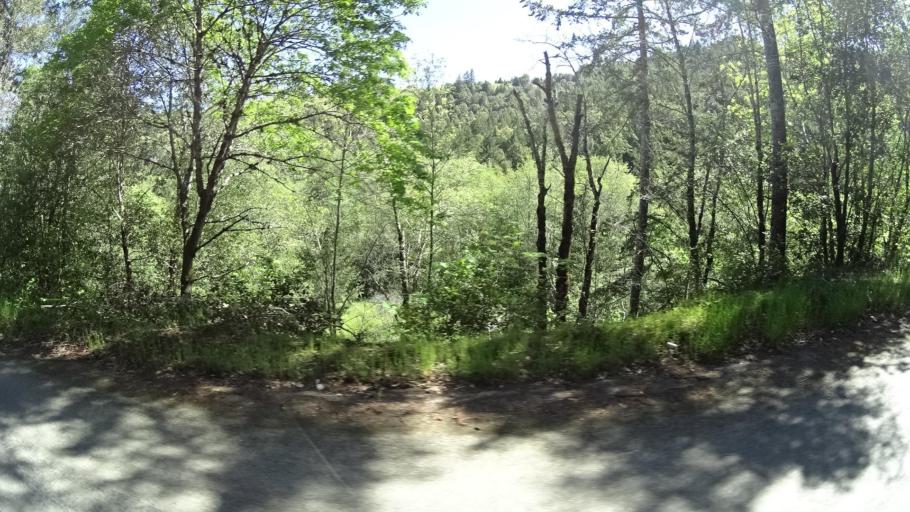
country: US
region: California
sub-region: Humboldt County
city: Rio Dell
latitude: 40.2284
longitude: -124.1104
